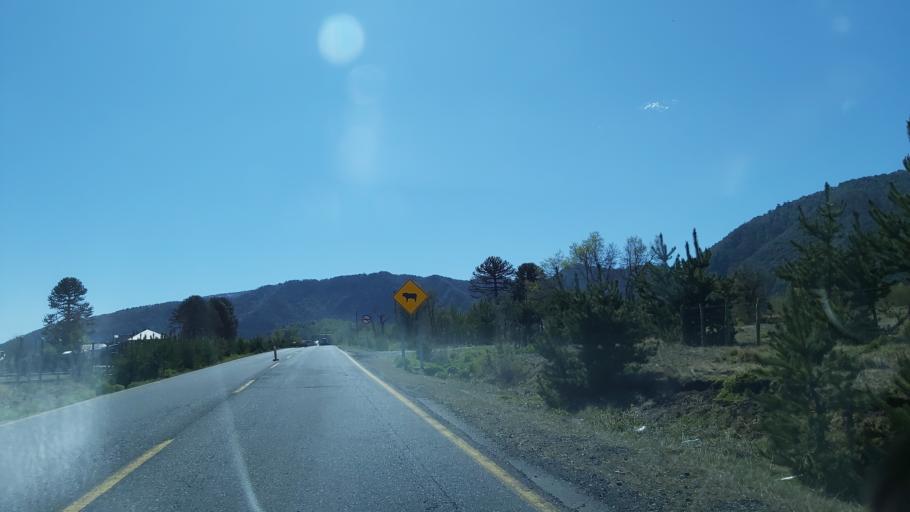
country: CL
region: Araucania
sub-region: Provincia de Cautin
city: Vilcun
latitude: -38.4665
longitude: -71.6024
